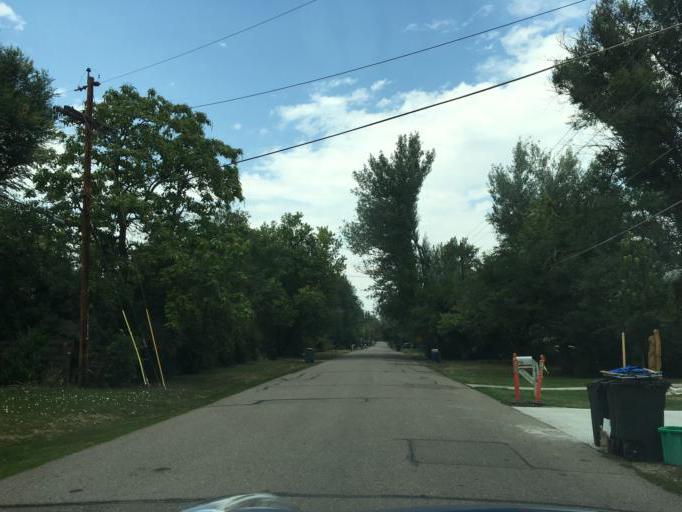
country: US
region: Colorado
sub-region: Jefferson County
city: Wheat Ridge
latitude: 39.7451
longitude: -105.0931
